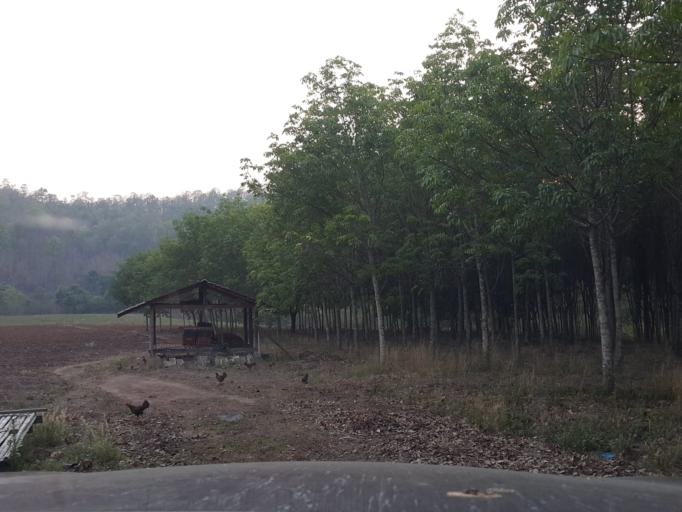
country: TH
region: Lamphun
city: Thung Hua Chang
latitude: 17.9179
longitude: 99.0714
